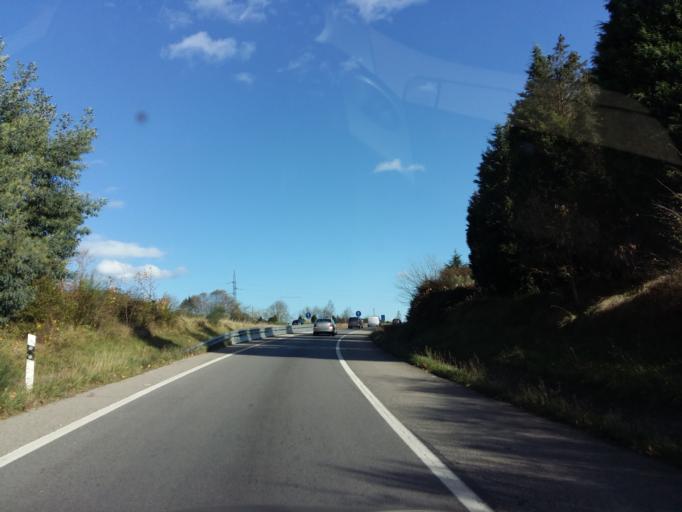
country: ES
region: Asturias
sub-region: Province of Asturias
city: Lugones
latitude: 43.3940
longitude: -5.8010
